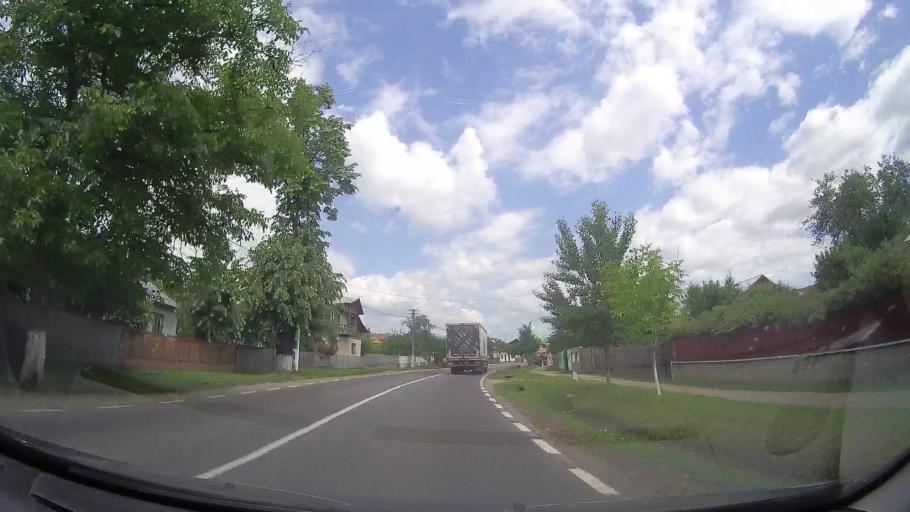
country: RO
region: Prahova
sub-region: Comuna Izvoarele
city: Homoraciu
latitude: 45.2654
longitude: 26.0142
